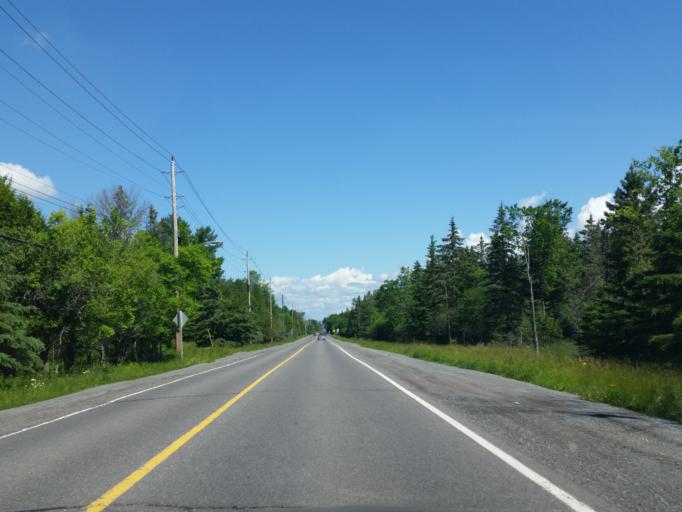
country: CA
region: Ontario
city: Bells Corners
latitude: 45.3066
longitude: -75.8241
